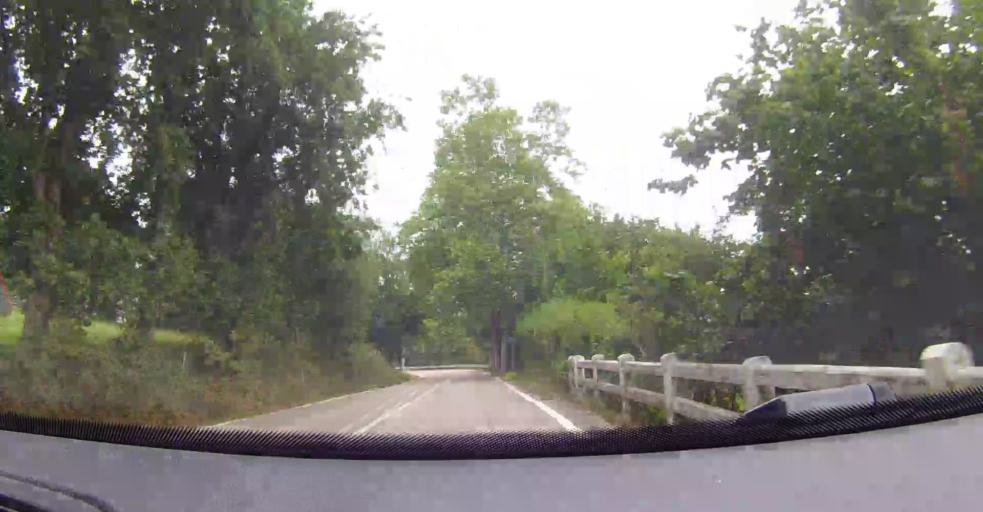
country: ES
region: Basque Country
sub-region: Bizkaia
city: Balmaseda
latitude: 43.2510
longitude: -3.2748
